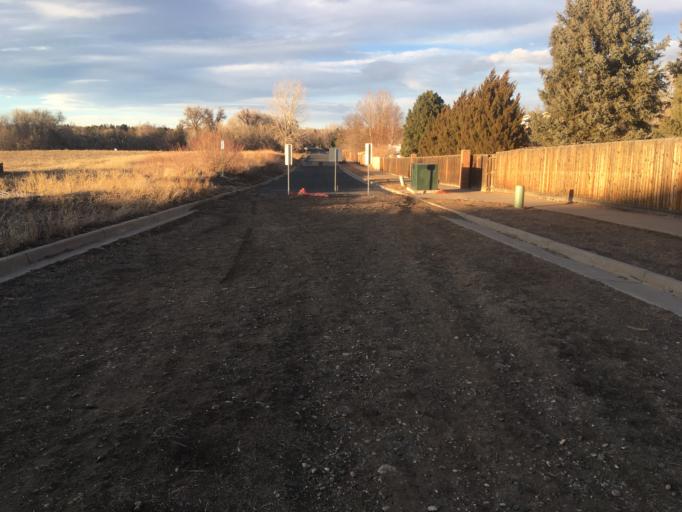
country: US
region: Colorado
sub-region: Jefferson County
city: Applewood
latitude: 39.8196
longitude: -105.1566
